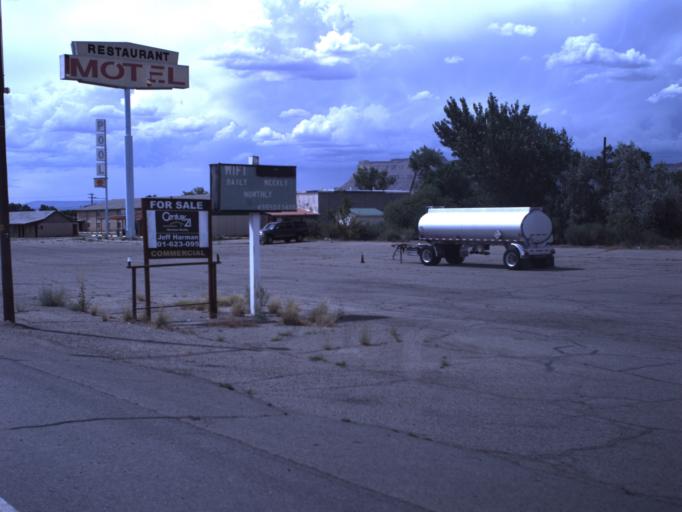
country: US
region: Utah
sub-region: Carbon County
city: East Carbon City
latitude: 38.9954
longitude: -110.1522
